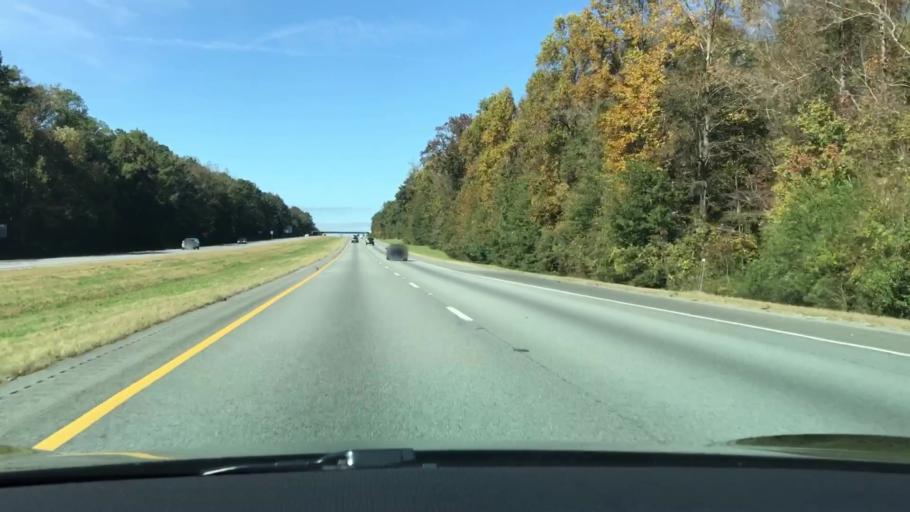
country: US
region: Georgia
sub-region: Morgan County
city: Madison
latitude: 33.5647
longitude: -83.5063
